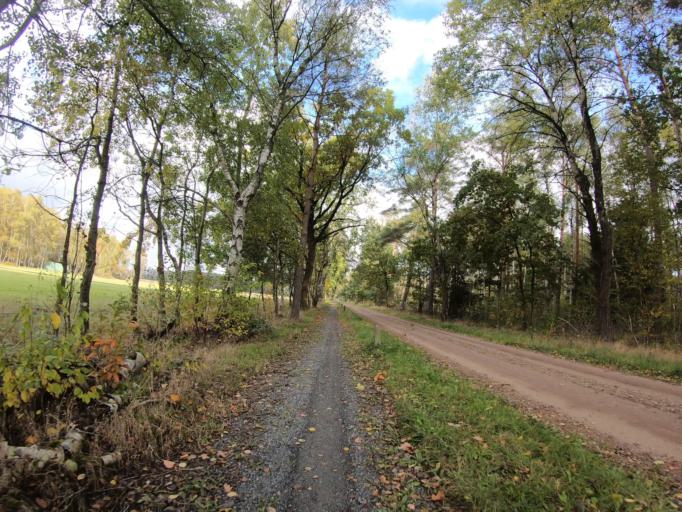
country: DE
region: Lower Saxony
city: Wesendorf
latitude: 52.5592
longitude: 10.5585
